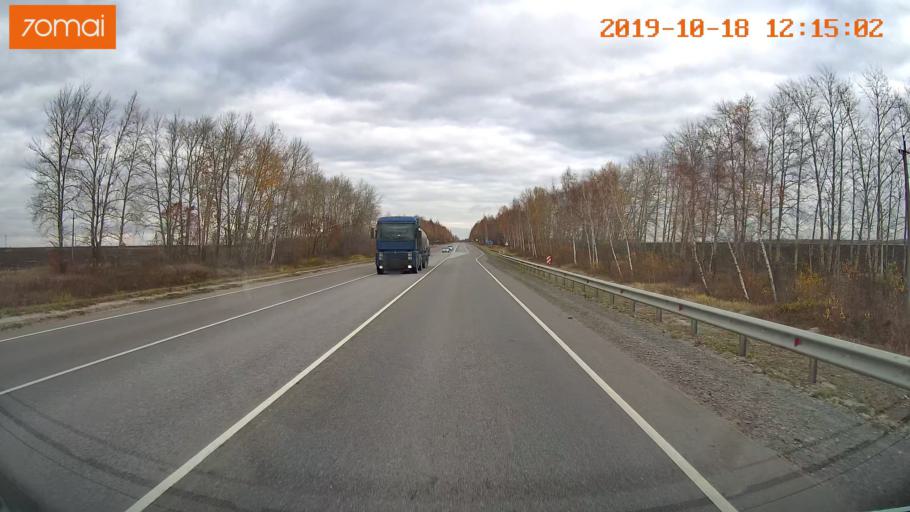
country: RU
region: Rjazan
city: Zakharovo
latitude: 54.4384
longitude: 39.3933
